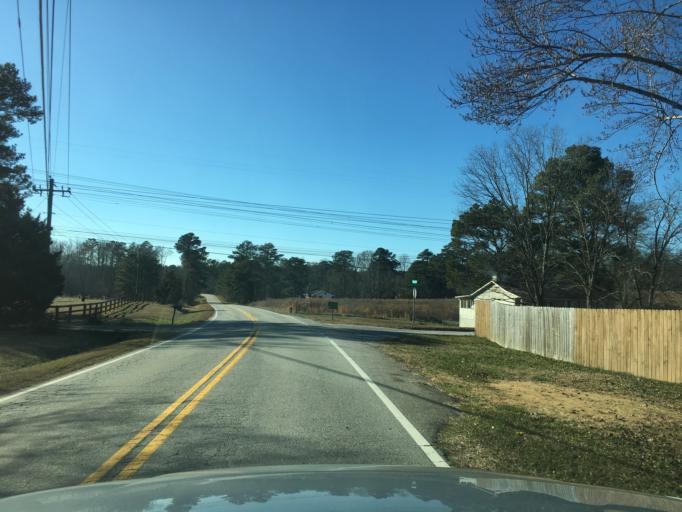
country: US
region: Georgia
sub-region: Carroll County
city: Villa Rica
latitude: 33.7118
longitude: -84.8466
